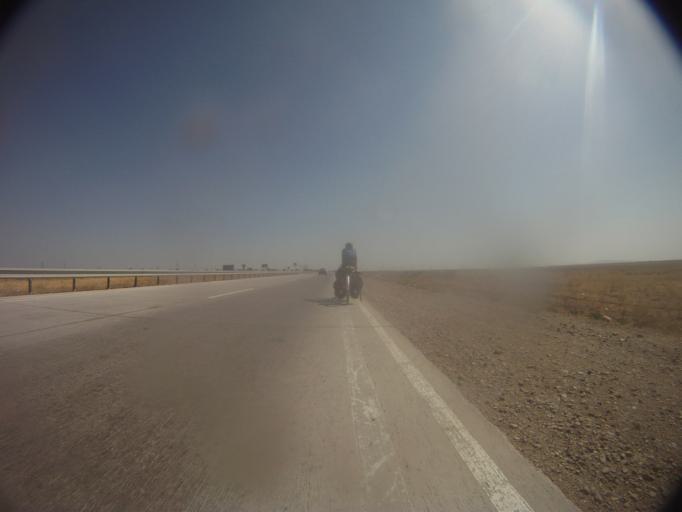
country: KZ
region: Zhambyl
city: Taraz
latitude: 42.7945
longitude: 71.0791
